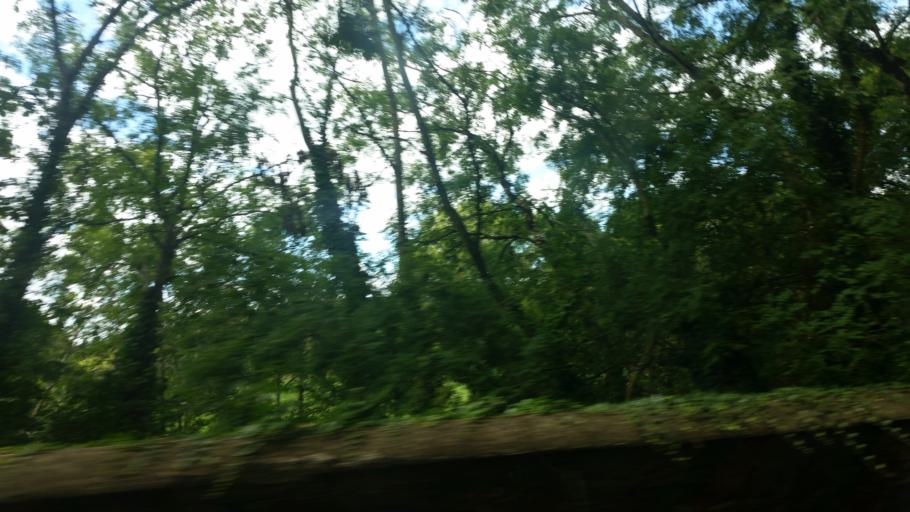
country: IE
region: Munster
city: Carrick-on-Suir
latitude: 52.2757
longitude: -7.4397
